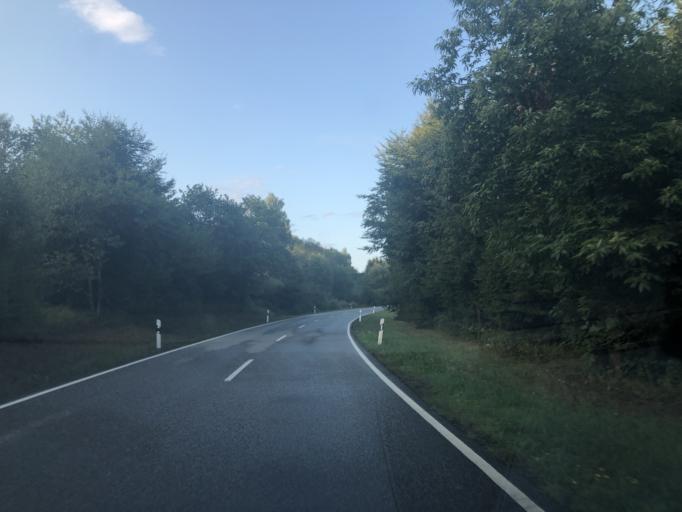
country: DE
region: Rheinland-Pfalz
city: Grimburg
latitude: 49.5972
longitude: 6.9067
